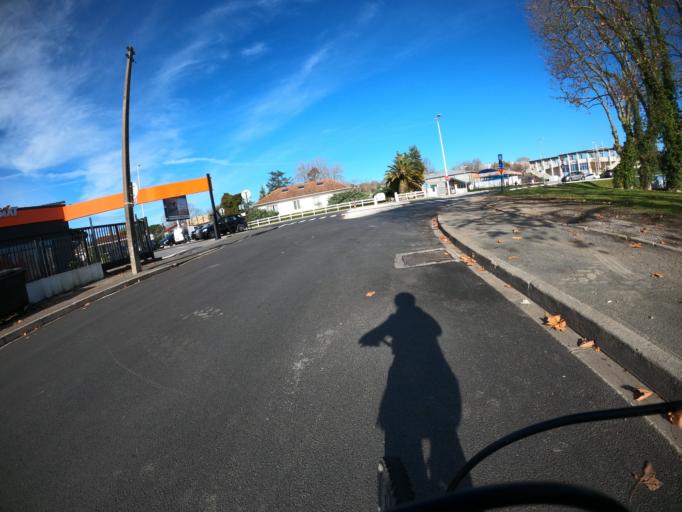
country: FR
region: Aquitaine
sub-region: Departement des Pyrenees-Atlantiques
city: Bayonne
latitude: 43.4934
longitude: -1.4576
